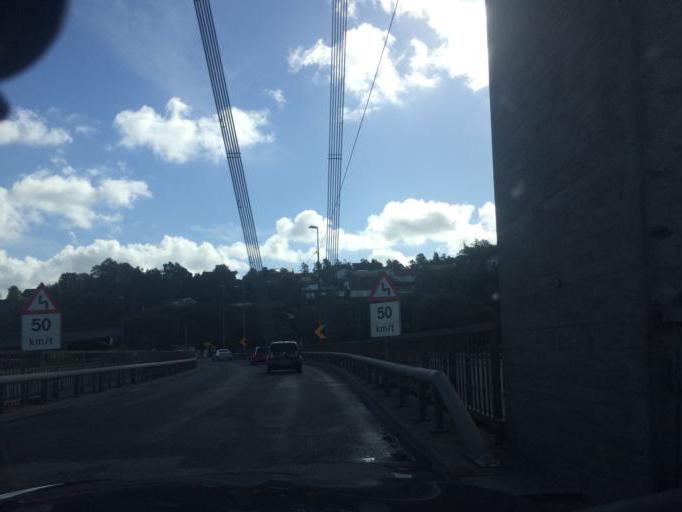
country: NO
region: Vest-Agder
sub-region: Kristiansand
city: Justvik
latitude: 58.1607
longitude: 8.0591
